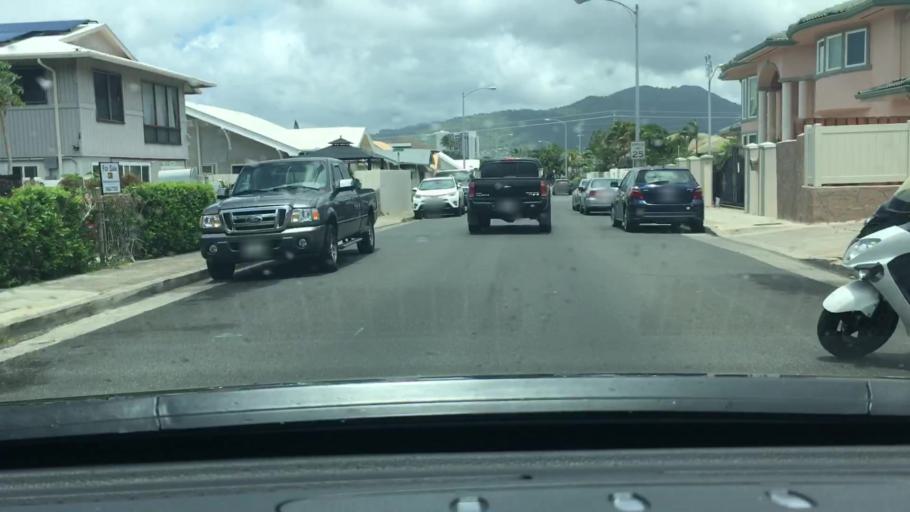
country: US
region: Hawaii
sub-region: Honolulu County
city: Honolulu
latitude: 21.2700
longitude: -157.8133
